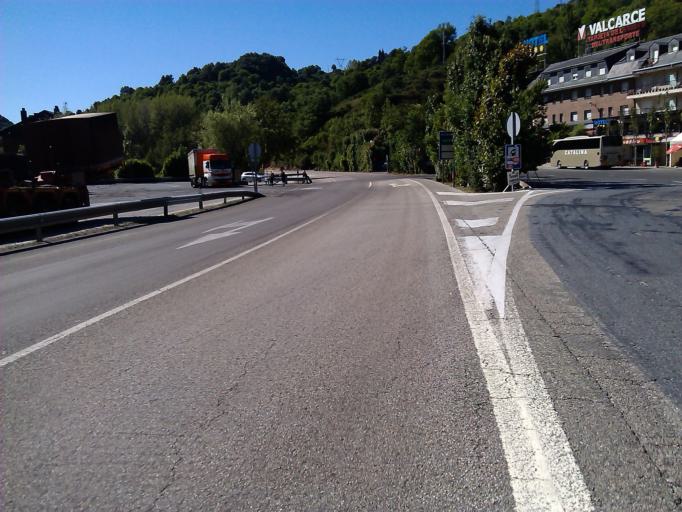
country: ES
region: Castille and Leon
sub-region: Provincia de Leon
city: Vega de Valcarce
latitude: 42.6587
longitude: -6.9146
